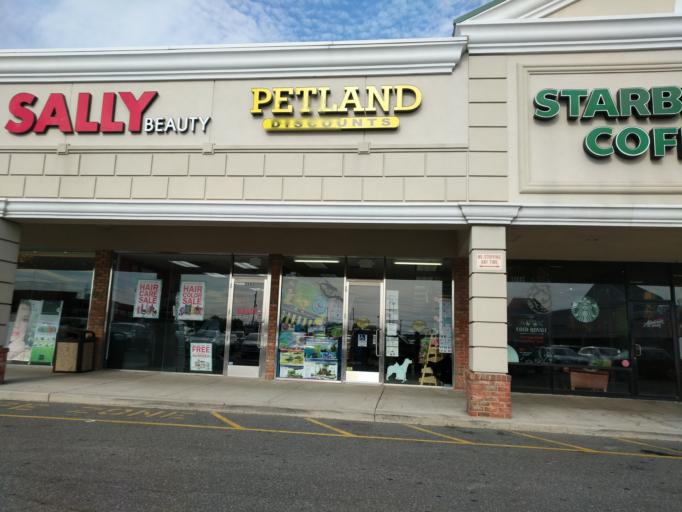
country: US
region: New York
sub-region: Nassau County
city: Oceanside
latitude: 40.6234
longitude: -73.6382
